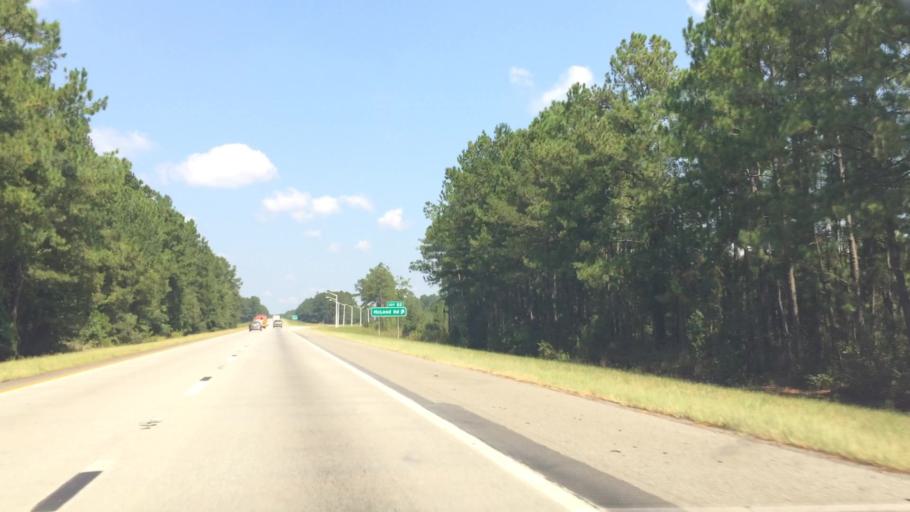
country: US
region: South Carolina
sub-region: Colleton County
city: Walterboro
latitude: 32.9959
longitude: -80.6705
